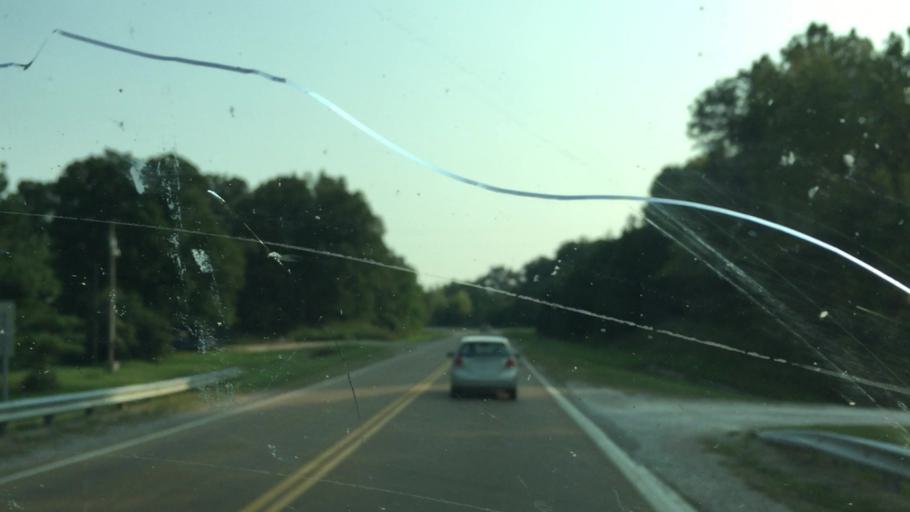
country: US
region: Missouri
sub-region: Pulaski County
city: Richland
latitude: 37.8194
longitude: -92.4061
